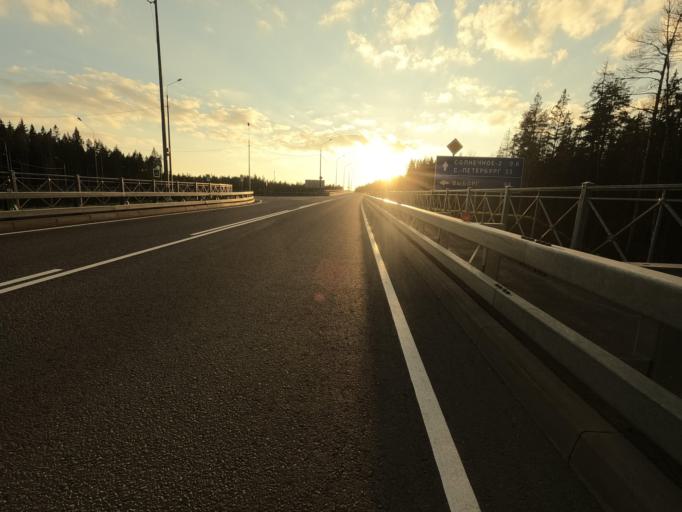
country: RU
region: St.-Petersburg
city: Solnechnoye
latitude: 60.1707
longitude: 29.9750
